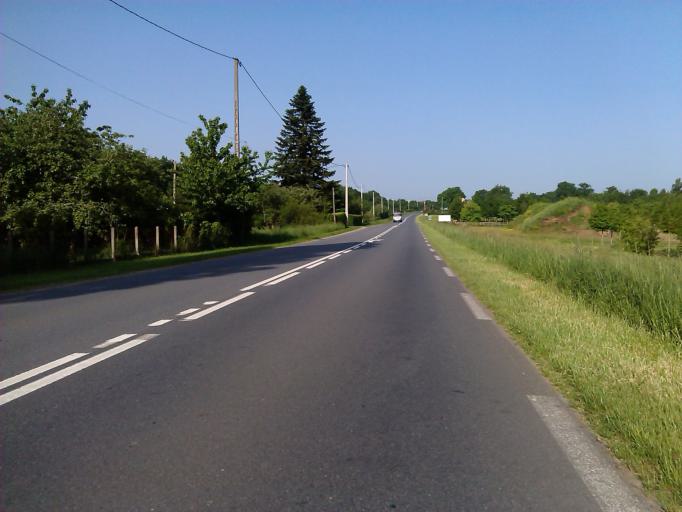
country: FR
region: Centre
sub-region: Departement de l'Indre
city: La Chatre
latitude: 46.5721
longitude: 1.9281
